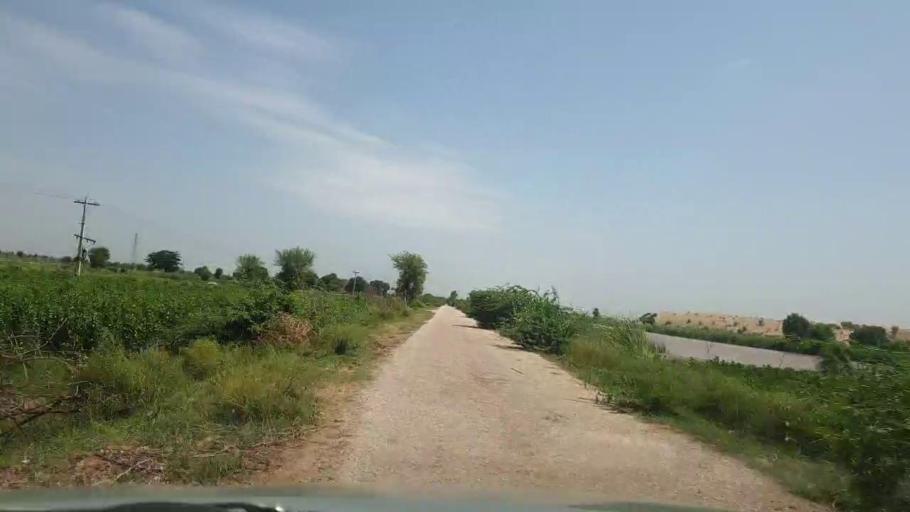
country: PK
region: Sindh
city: Bozdar
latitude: 27.0963
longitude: 68.9726
